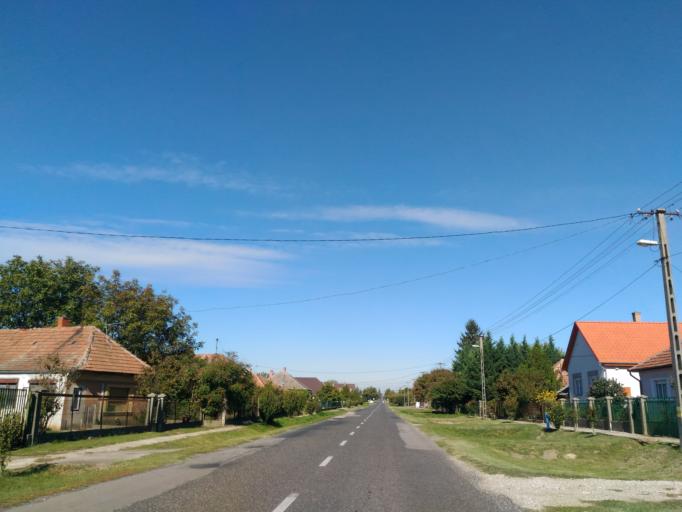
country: HU
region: Fejer
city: Ivancsa
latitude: 47.1641
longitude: 18.8236
